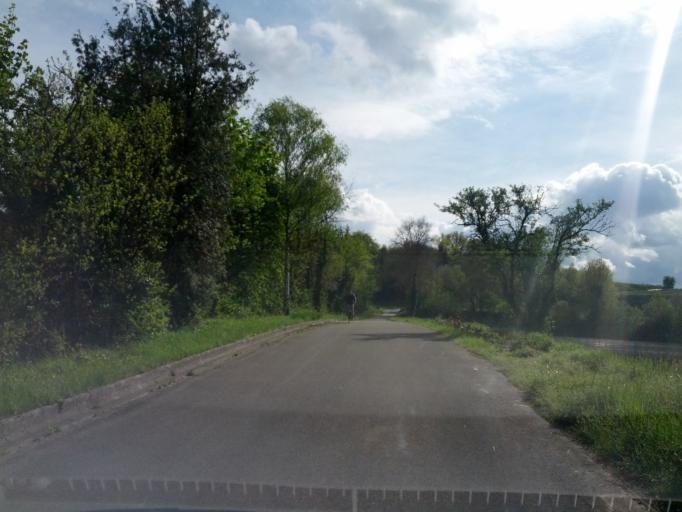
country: DE
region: Baden-Wuerttemberg
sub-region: Freiburg Region
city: Merdingen
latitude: 47.9696
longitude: 7.6914
